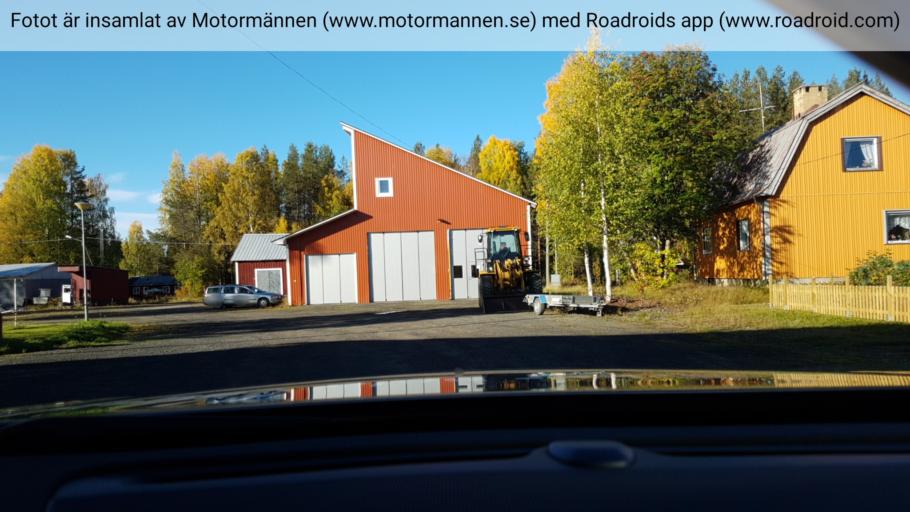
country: SE
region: Norrbotten
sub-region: Alvsbyns Kommun
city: AElvsbyn
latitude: 66.2764
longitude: 21.1230
